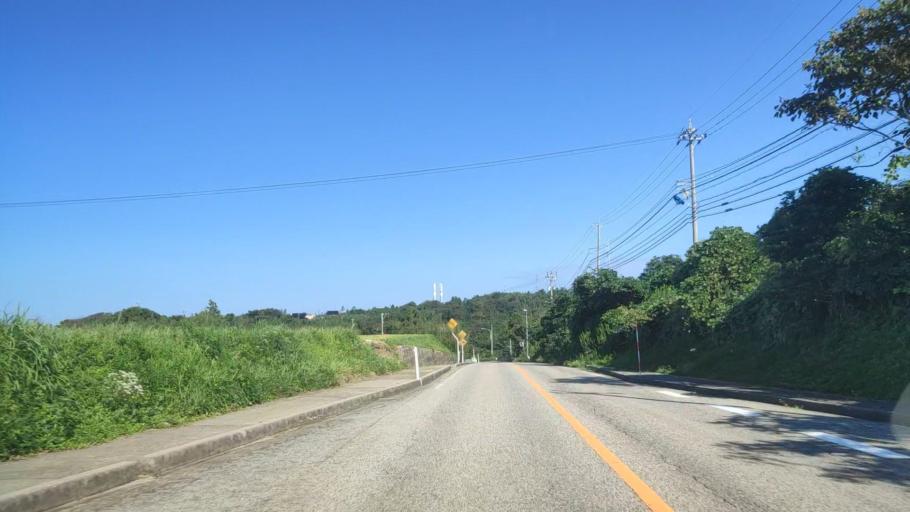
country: JP
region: Ishikawa
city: Hakui
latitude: 37.0492
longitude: 136.7362
